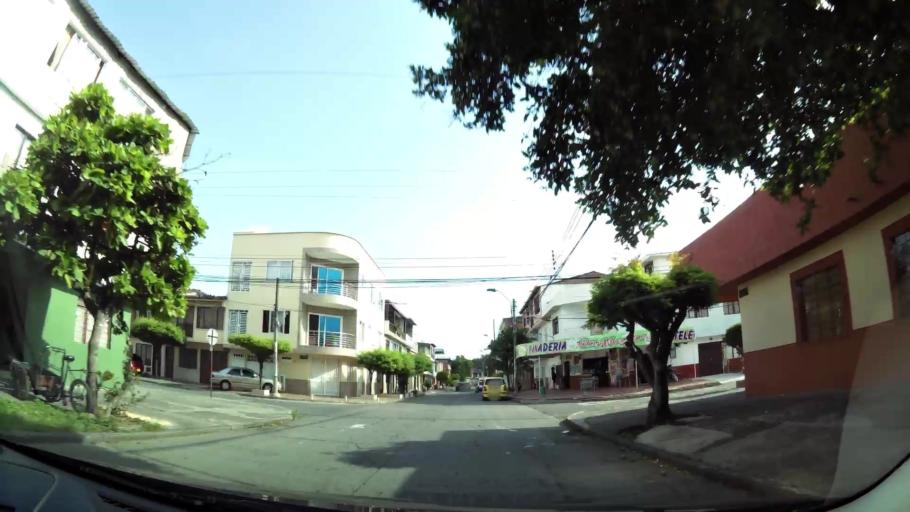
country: CO
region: Valle del Cauca
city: Cali
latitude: 3.4200
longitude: -76.5258
